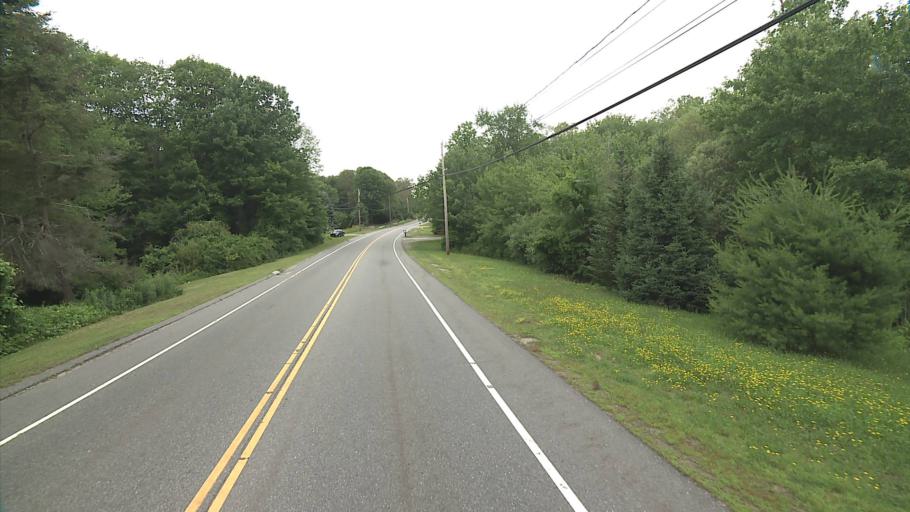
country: US
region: Connecticut
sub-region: New London County
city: Ledyard Center
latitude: 41.4328
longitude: -72.0141
